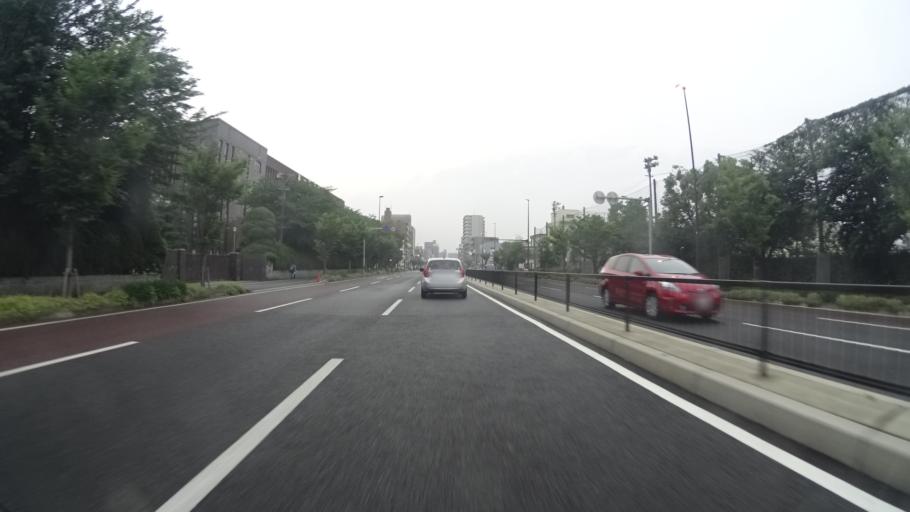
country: JP
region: Fukuoka
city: Fukuoka-shi
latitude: 33.5655
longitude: 130.4214
